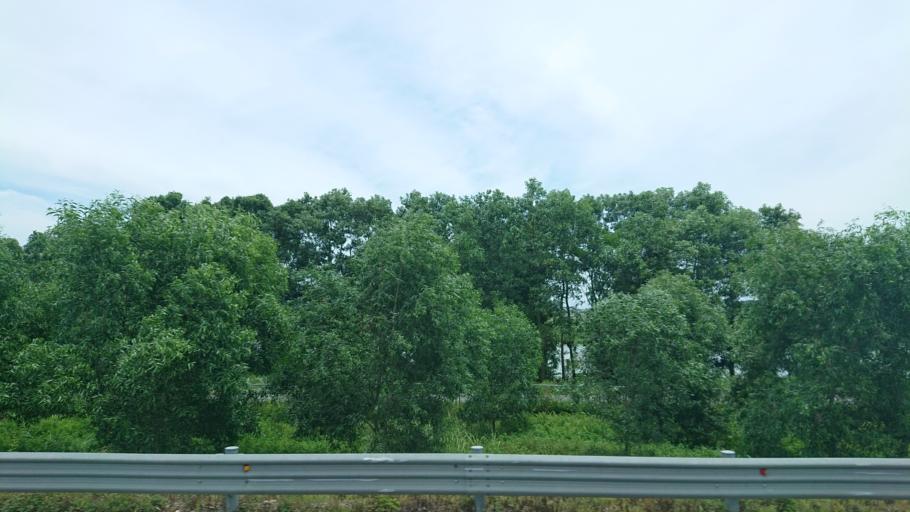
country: VN
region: Hai Phong
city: Tien Lang
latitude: 20.7709
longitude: 106.5938
